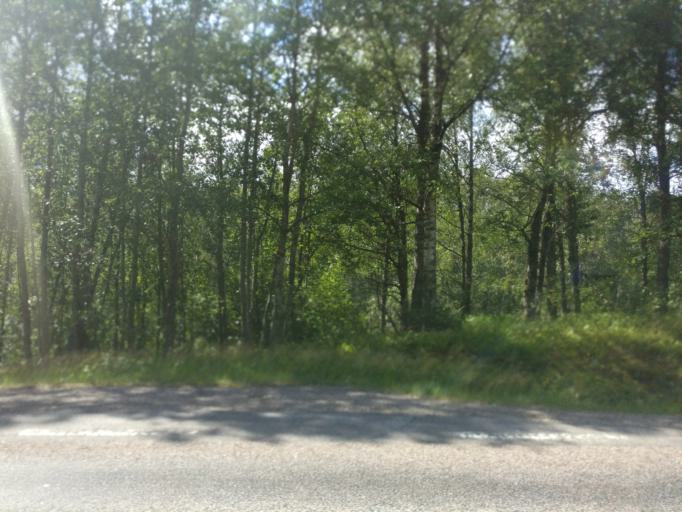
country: SE
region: Vaermland
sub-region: Hagfors Kommun
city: Ekshaerad
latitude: 60.3696
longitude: 13.3050
